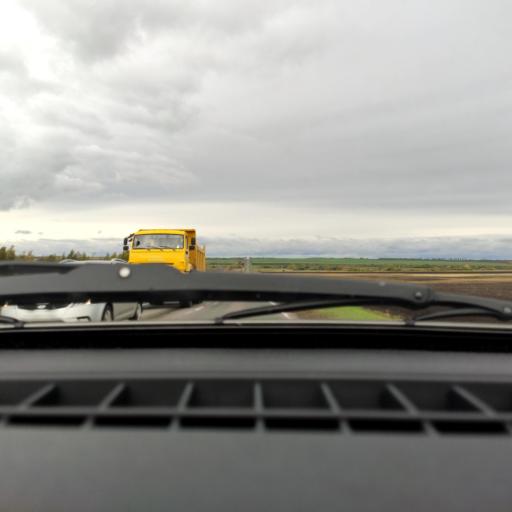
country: RU
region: Bashkortostan
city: Rayevskiy
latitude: 54.1220
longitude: 54.9322
